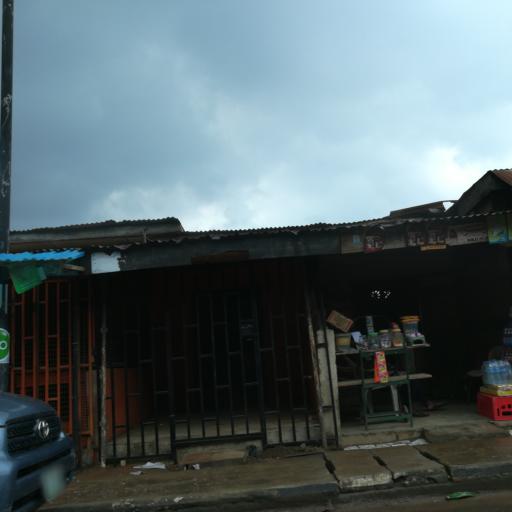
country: NG
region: Lagos
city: Agege
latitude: 6.5955
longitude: 3.2930
